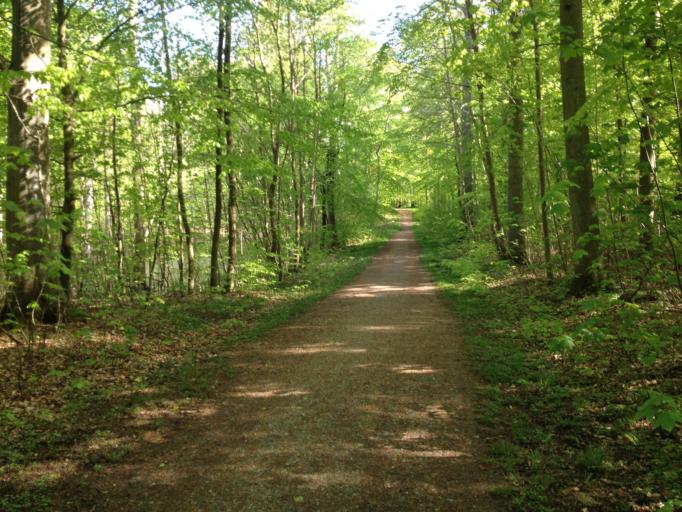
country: DK
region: Capital Region
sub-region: Fredensborg Kommune
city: Niva
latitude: 55.9443
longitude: 12.5206
